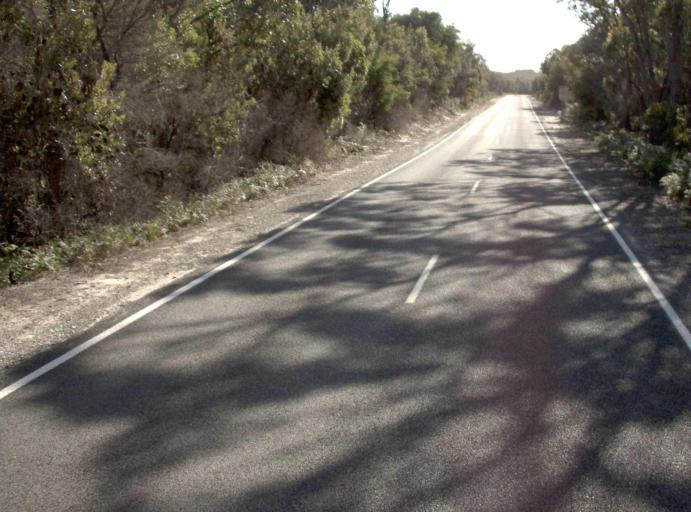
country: AU
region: Victoria
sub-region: East Gippsland
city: Lakes Entrance
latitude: -37.8007
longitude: 148.7317
